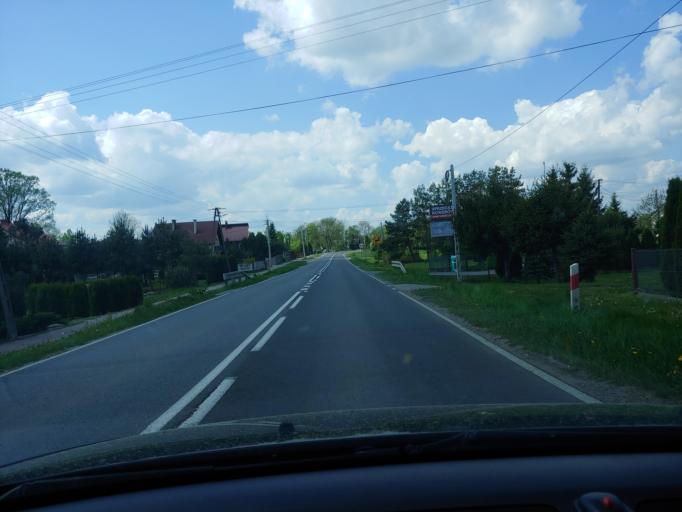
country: PL
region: Subcarpathian Voivodeship
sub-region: Powiat mielecki
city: Wadowice Gorne
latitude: 50.2393
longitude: 21.2937
